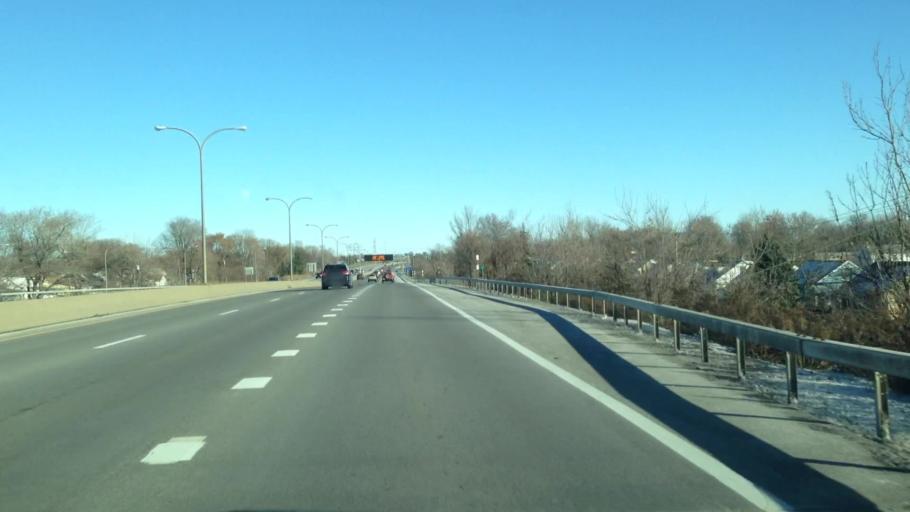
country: US
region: New York
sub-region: Erie County
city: Eggertsville
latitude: 42.9329
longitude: -78.7838
